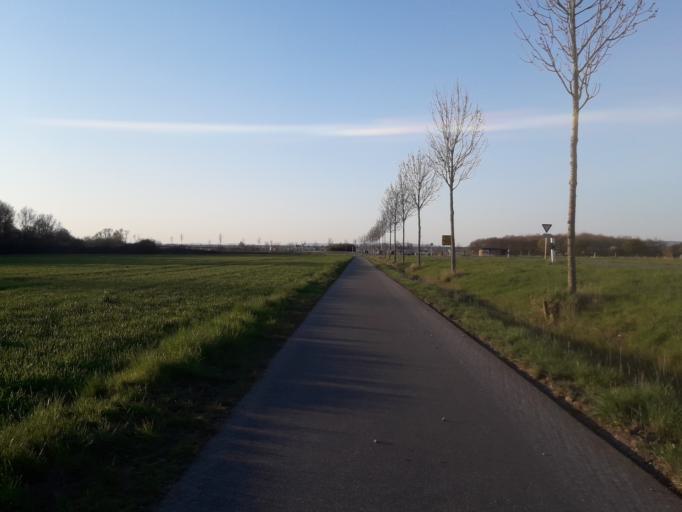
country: DE
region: North Rhine-Westphalia
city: Bad Lippspringe
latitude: 51.7527
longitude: 8.8340
